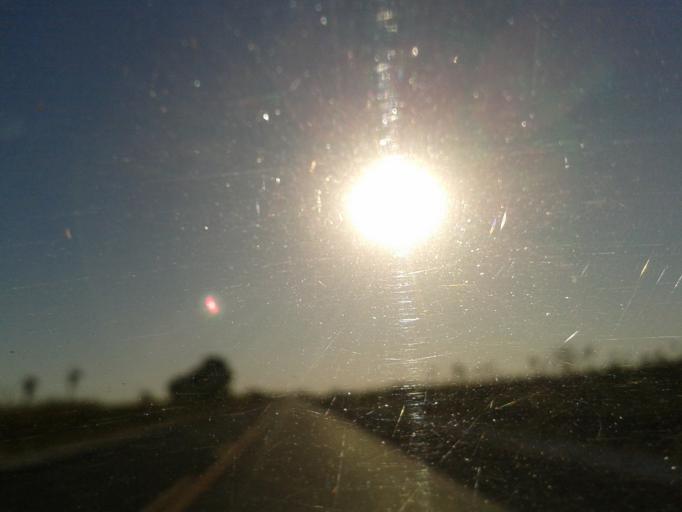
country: BR
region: Minas Gerais
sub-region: Santa Vitoria
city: Santa Vitoria
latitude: -19.1196
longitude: -50.3032
